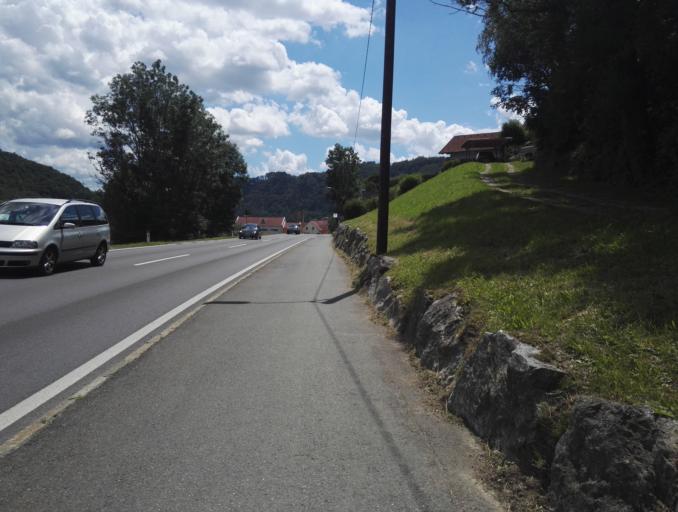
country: AT
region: Styria
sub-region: Politischer Bezirk Graz-Umgebung
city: Gratkorn
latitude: 47.1172
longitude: 15.3685
